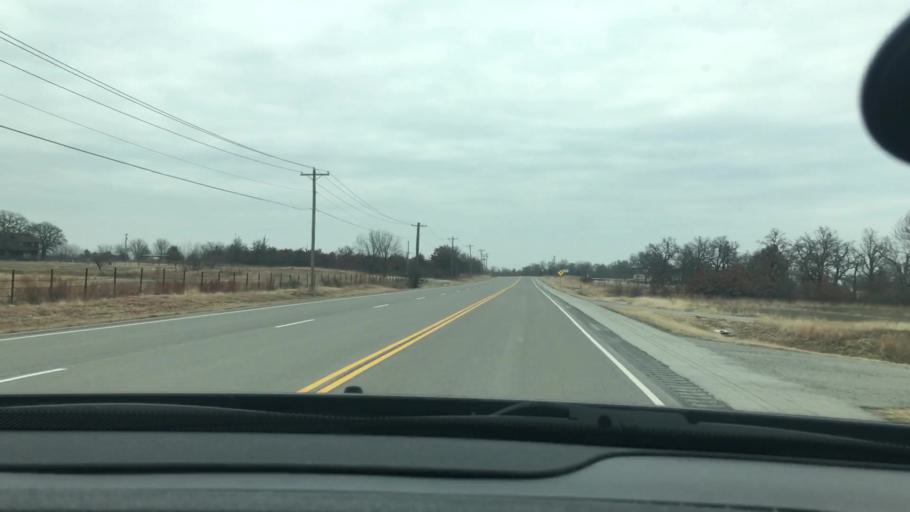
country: US
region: Oklahoma
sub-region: Carter County
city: Healdton
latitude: 34.3959
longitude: -97.5035
